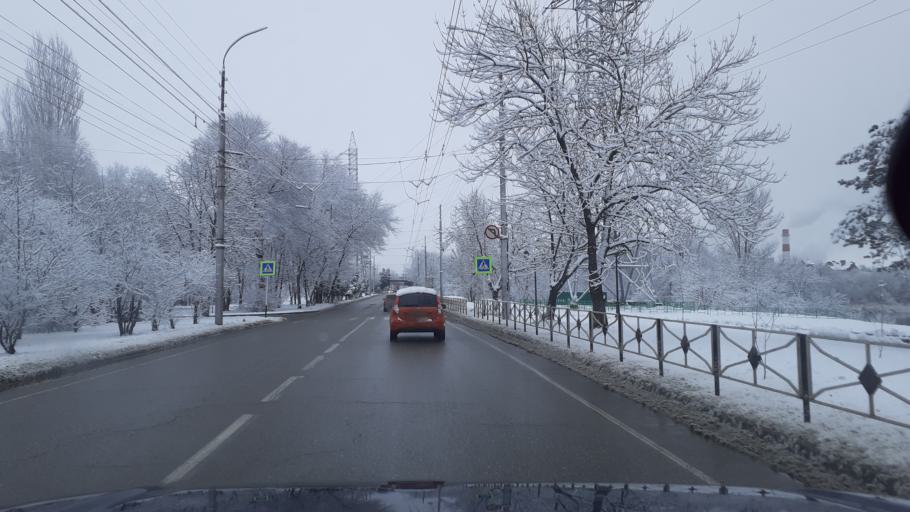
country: RU
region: Adygeya
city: Maykop
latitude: 44.5911
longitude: 40.1166
